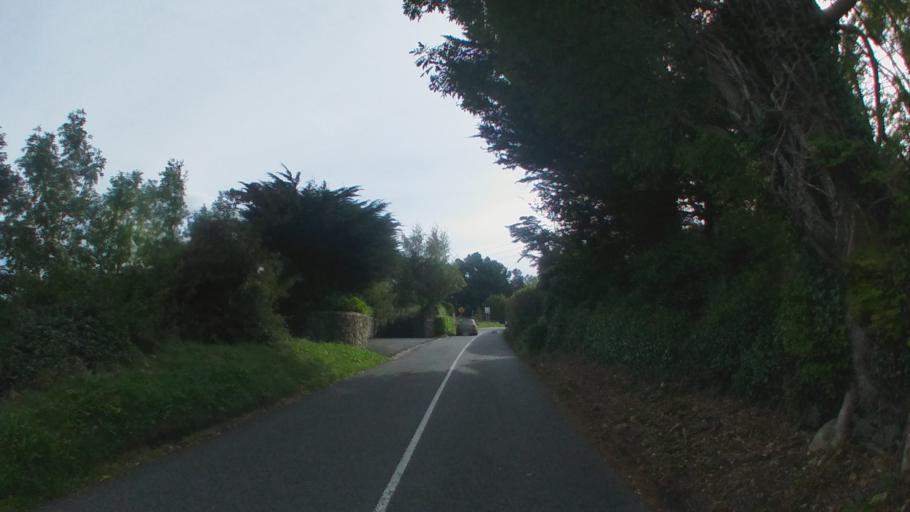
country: IE
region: Leinster
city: Sandyford
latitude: 53.2482
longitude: -6.2171
